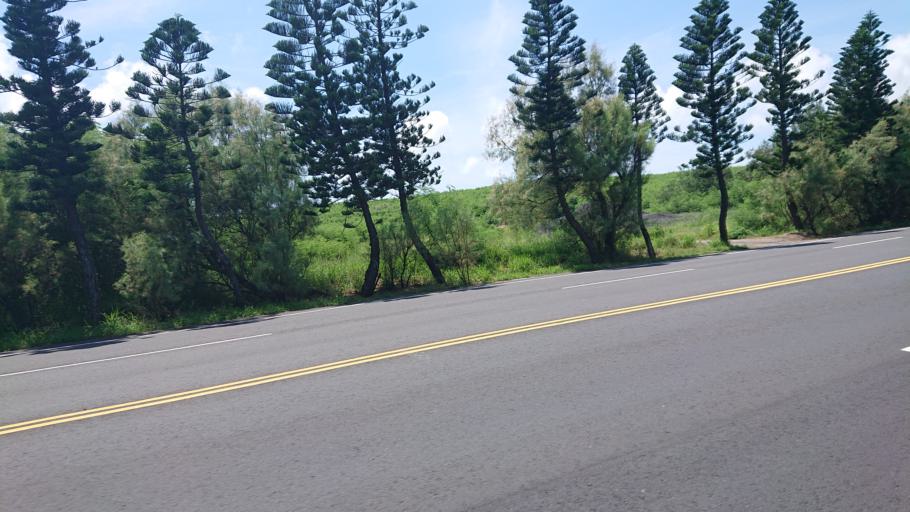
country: TW
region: Taiwan
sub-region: Penghu
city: Ma-kung
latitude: 23.6379
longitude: 119.5972
